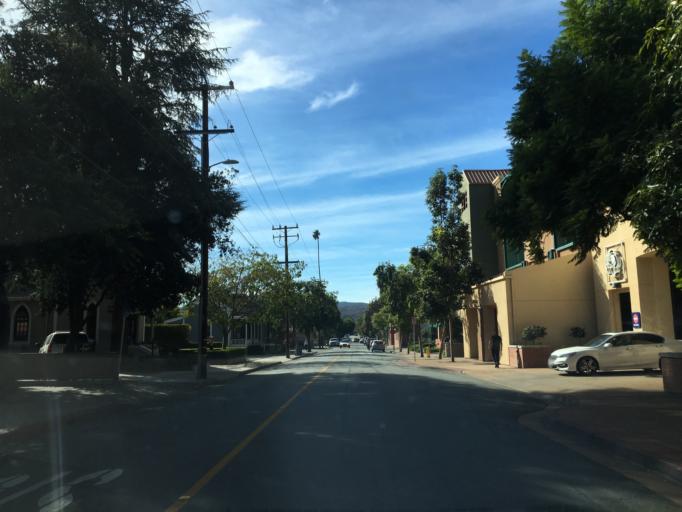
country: US
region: California
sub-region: San Luis Obispo County
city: San Luis Obispo
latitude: 35.2790
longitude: -120.6607
